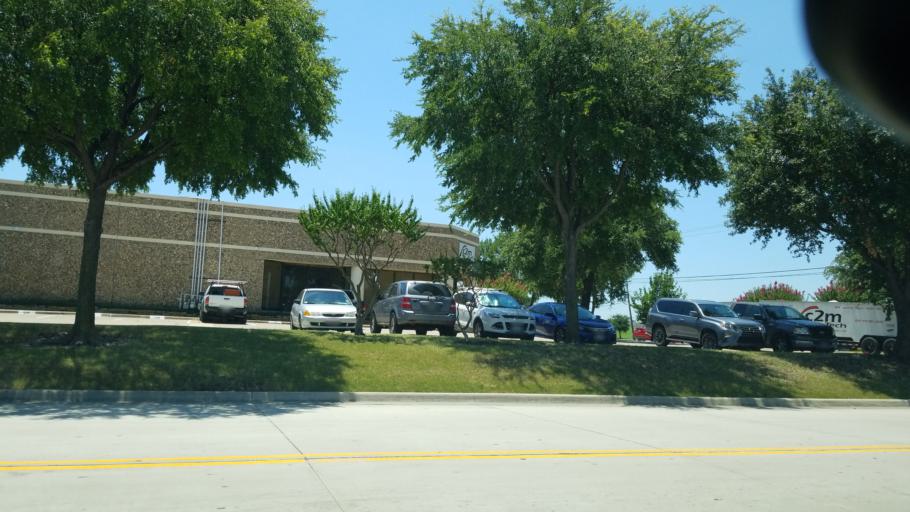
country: US
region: Texas
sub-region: Dallas County
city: Farmers Branch
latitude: 32.9266
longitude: -96.9248
